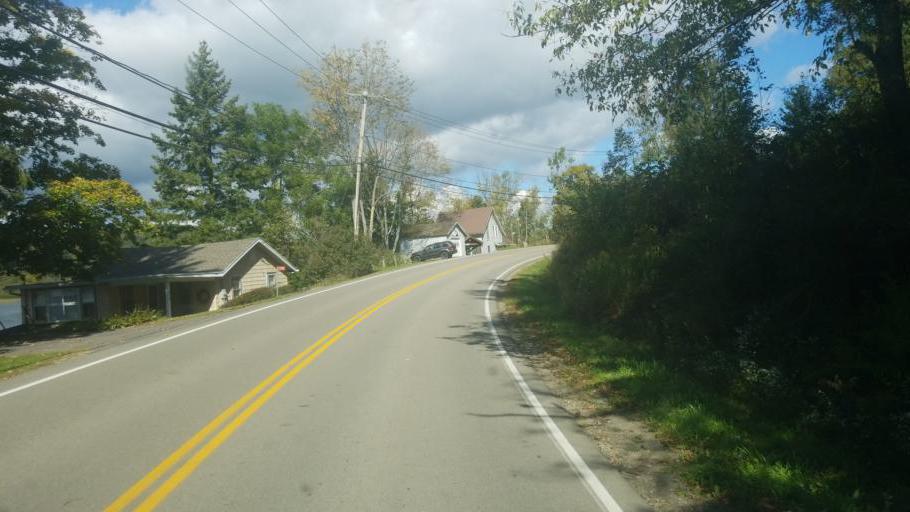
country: US
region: New York
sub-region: Allegany County
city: Cuba
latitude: 42.2563
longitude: -78.2919
